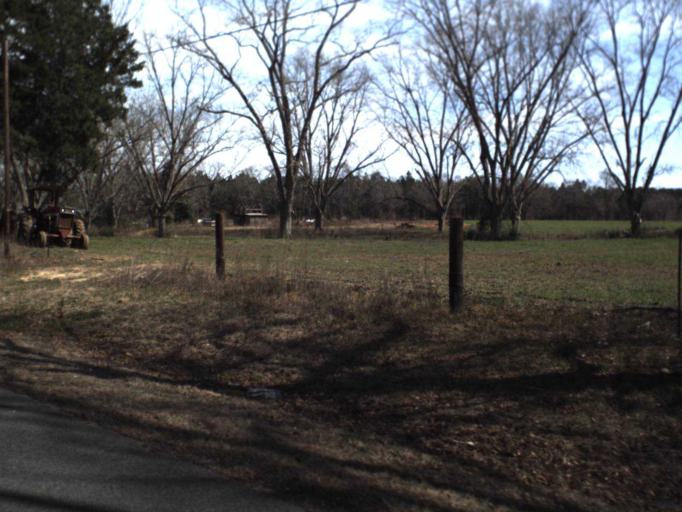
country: US
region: Florida
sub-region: Jackson County
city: Graceville
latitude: 30.9753
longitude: -85.4963
